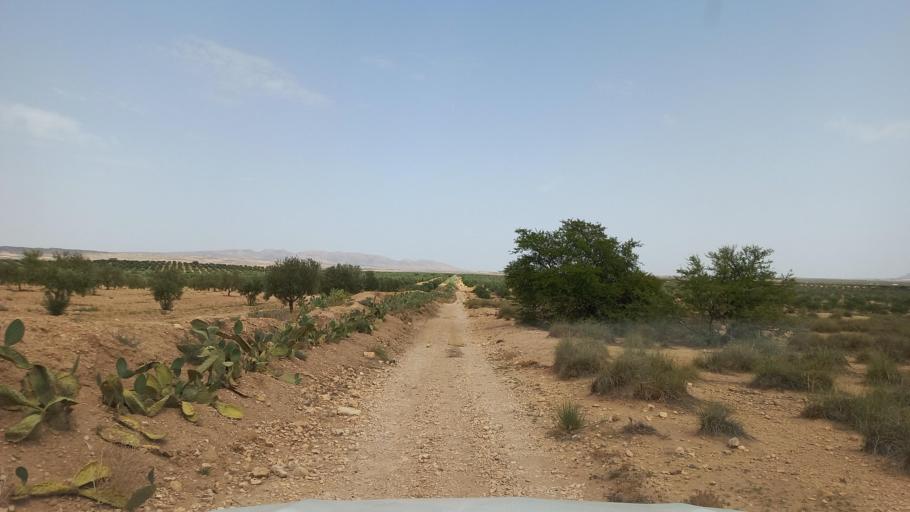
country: TN
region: Al Qasrayn
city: Kasserine
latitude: 35.2933
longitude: 9.0045
